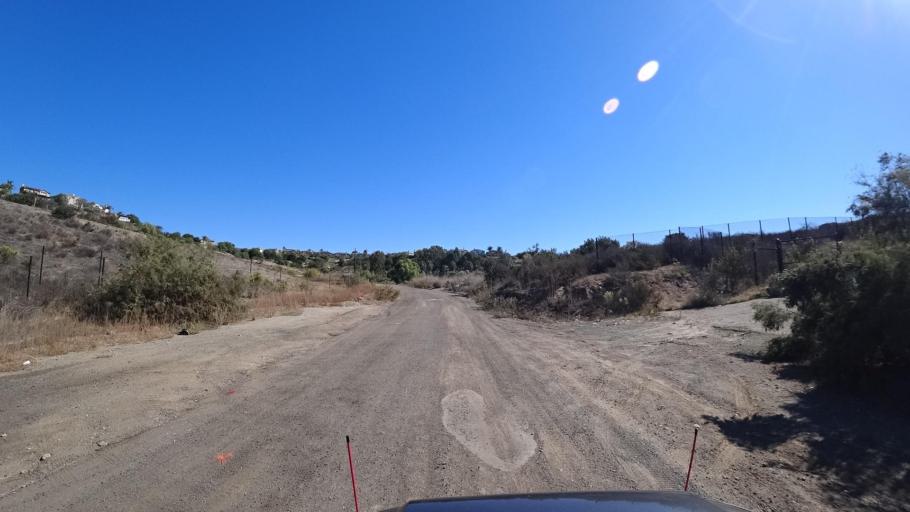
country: US
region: California
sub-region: San Diego County
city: La Presa
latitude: 32.6656
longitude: -116.9833
